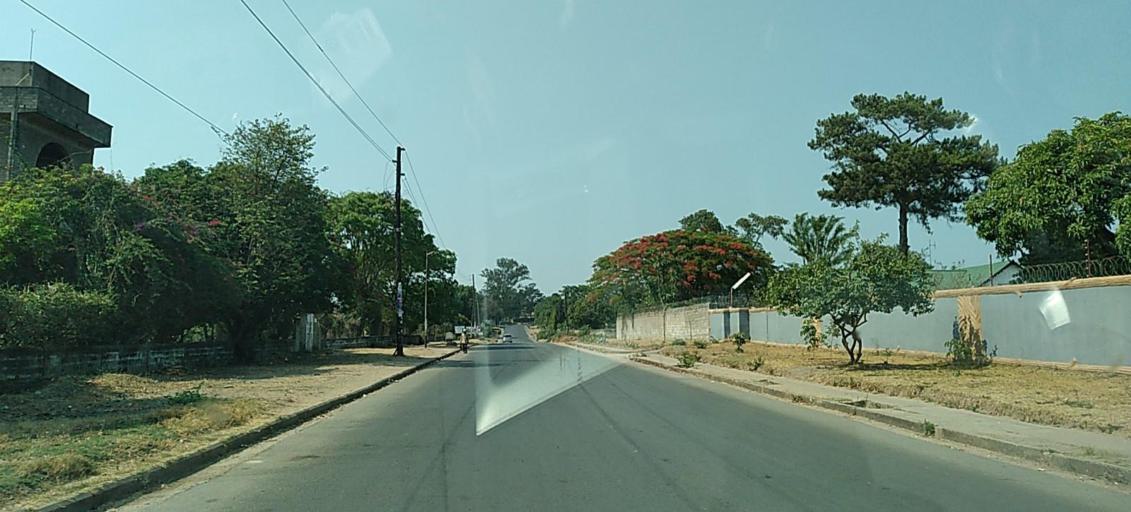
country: ZM
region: Copperbelt
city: Chingola
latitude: -12.5480
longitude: 27.8709
